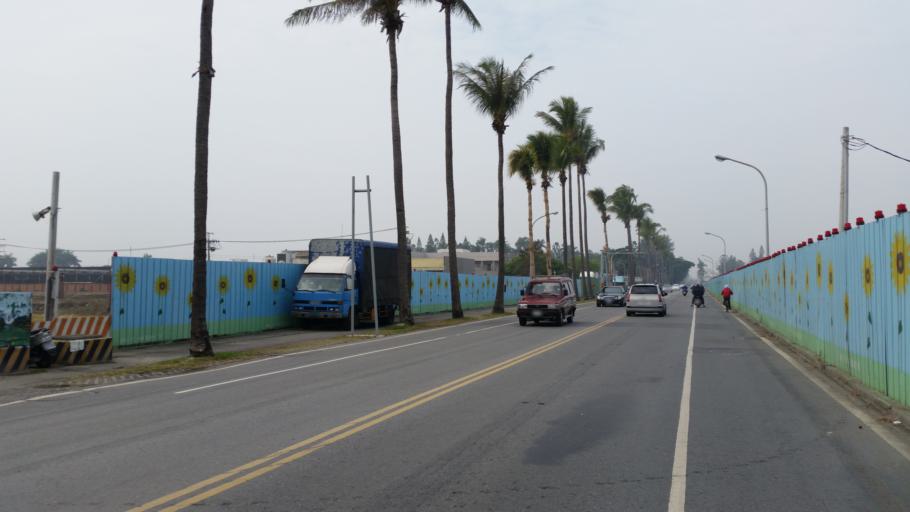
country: TW
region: Taiwan
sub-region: Tainan
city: Tainan
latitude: 22.9650
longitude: 120.2262
